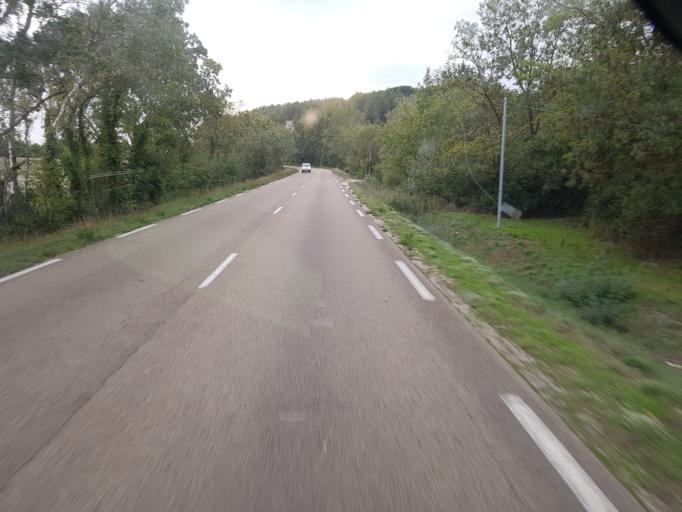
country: FR
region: Languedoc-Roussillon
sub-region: Departement du Gard
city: Les Angles
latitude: 43.9345
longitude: 4.7471
